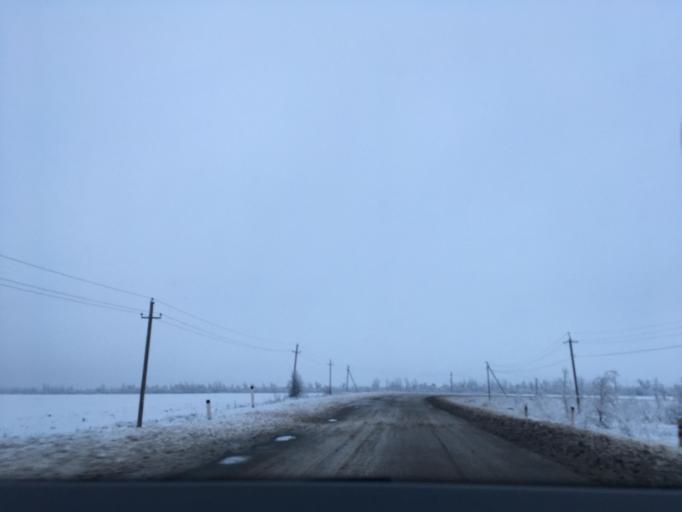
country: RU
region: Voronezj
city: Verkhniy Mamon
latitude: 50.0339
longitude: 40.0579
